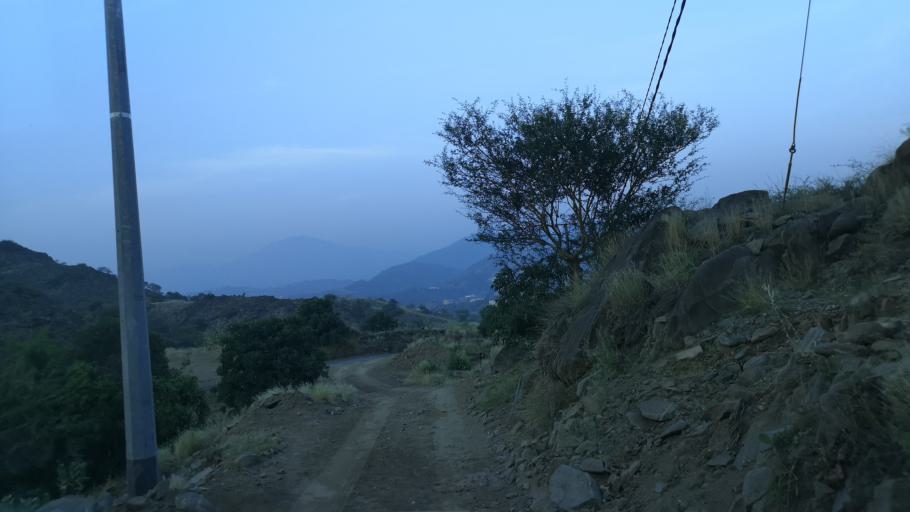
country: YE
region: Sa'dah
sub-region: Monabbih
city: Suq al Khamis
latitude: 17.3799
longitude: 43.1298
